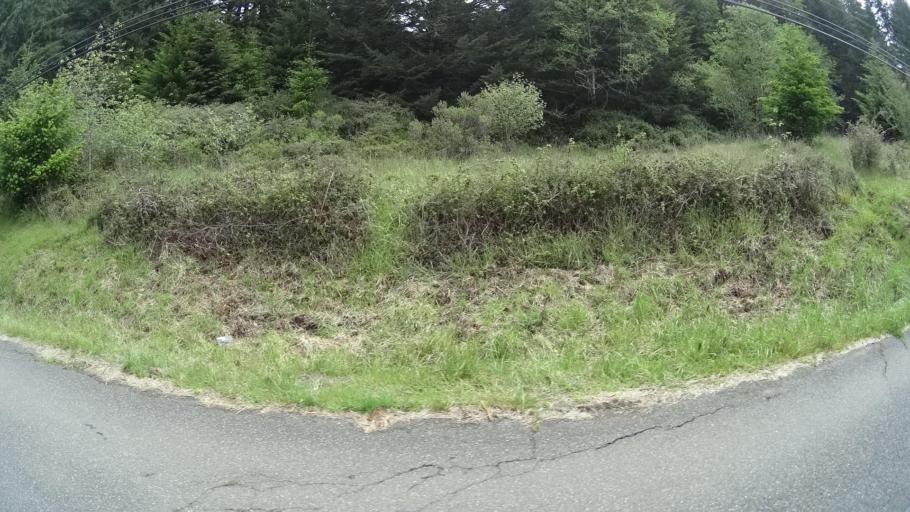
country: US
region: California
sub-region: Humboldt County
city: Bayside
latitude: 40.8409
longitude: -124.0250
